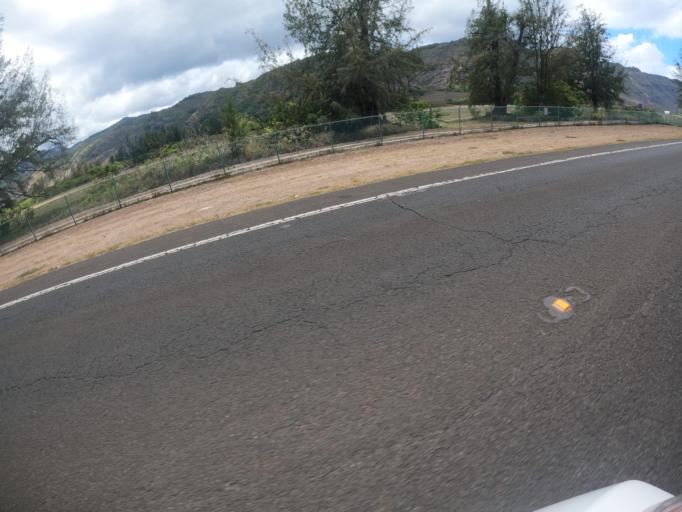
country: US
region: Hawaii
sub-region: Honolulu County
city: Mokuleia
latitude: 21.5811
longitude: -158.1981
